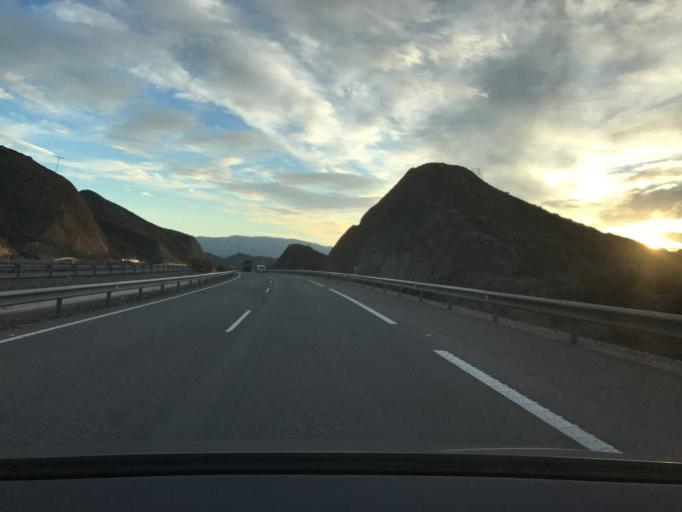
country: ES
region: Andalusia
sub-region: Provincia de Almeria
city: Rioja
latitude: 37.0002
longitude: -2.4620
